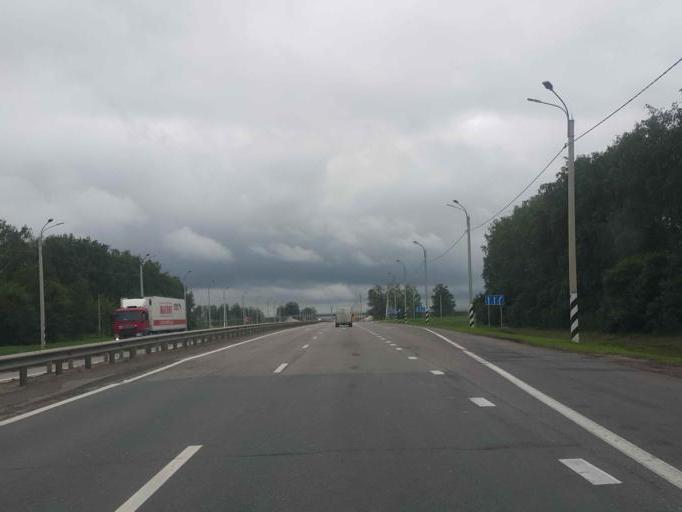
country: RU
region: Tambov
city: Komsomolets
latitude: 52.7370
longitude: 41.2592
